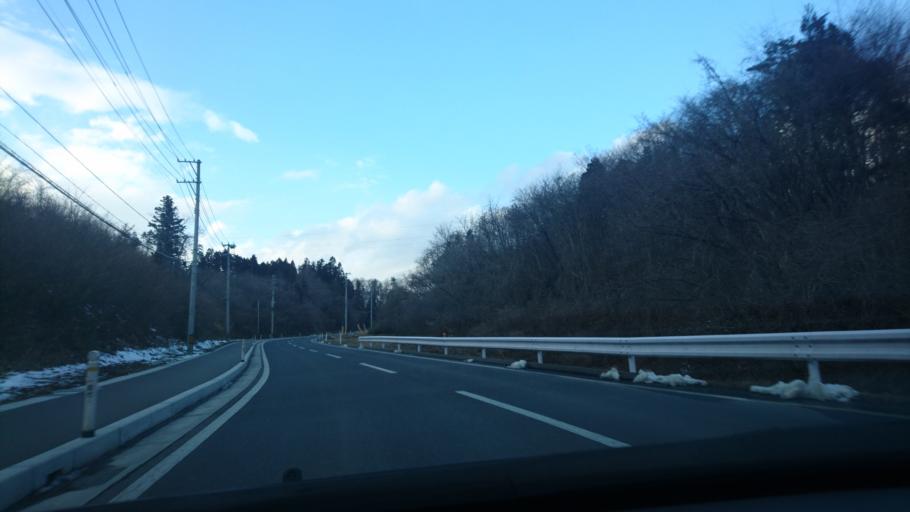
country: JP
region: Iwate
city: Ichinoseki
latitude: 39.0023
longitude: 141.3333
